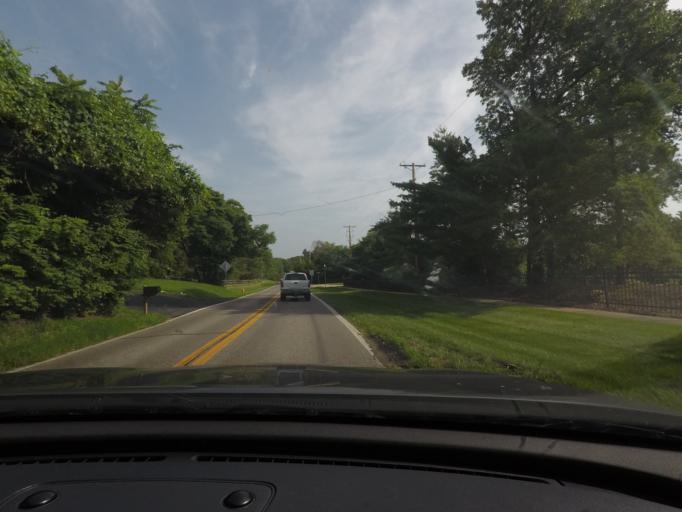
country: US
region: Missouri
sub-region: Saint Louis County
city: Town and Country
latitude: 38.6214
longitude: -90.4824
